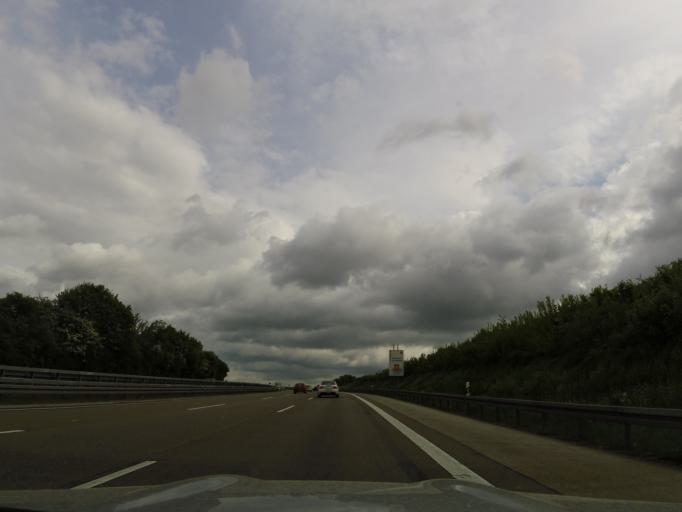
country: DE
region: Hesse
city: Bad Camberg
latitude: 50.2601
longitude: 8.2497
